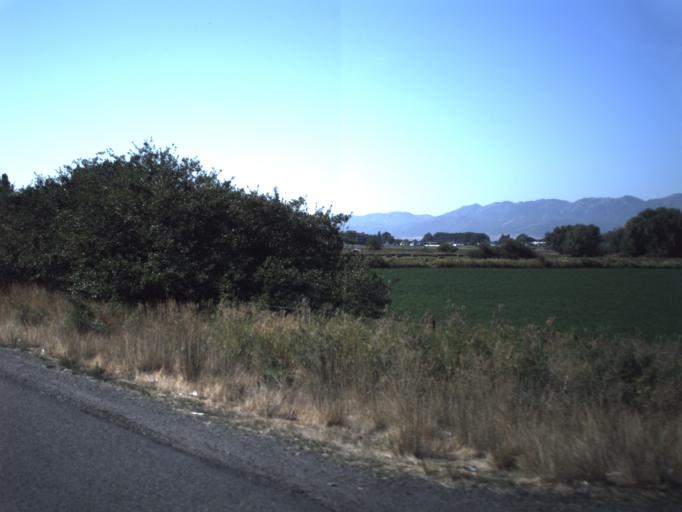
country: US
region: Utah
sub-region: Cache County
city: Providence
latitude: 41.6978
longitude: -111.8350
